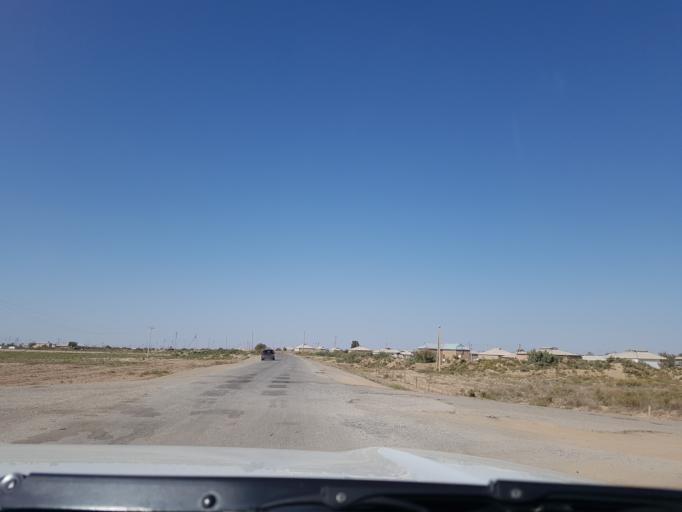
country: IR
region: Razavi Khorasan
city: Sarakhs
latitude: 36.5121
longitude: 61.2532
